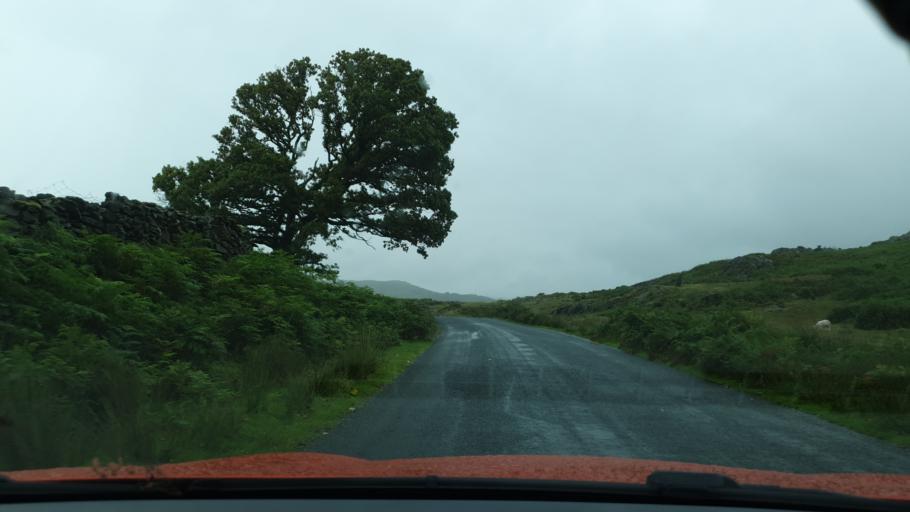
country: GB
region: England
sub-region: Cumbria
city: Millom
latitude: 54.3223
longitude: -3.2354
